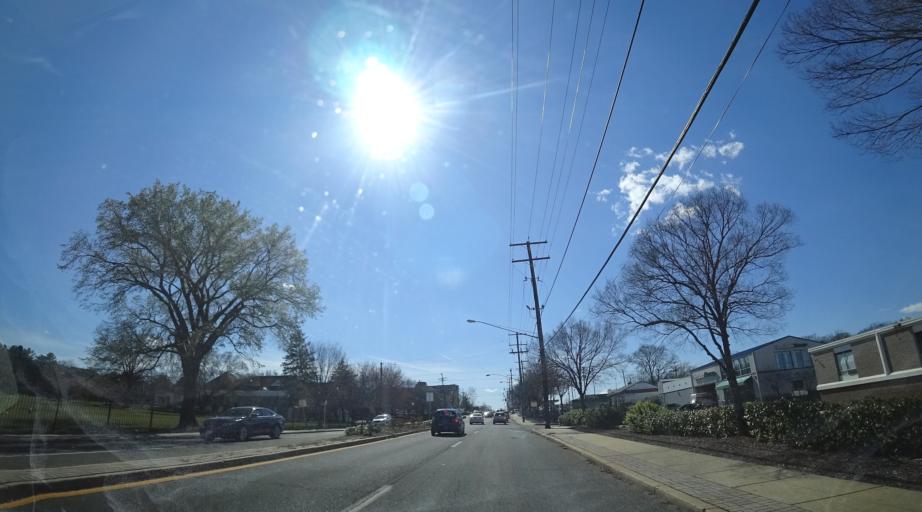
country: US
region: Maryland
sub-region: Prince George's County
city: Cottage City
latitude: 38.9318
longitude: -76.9564
